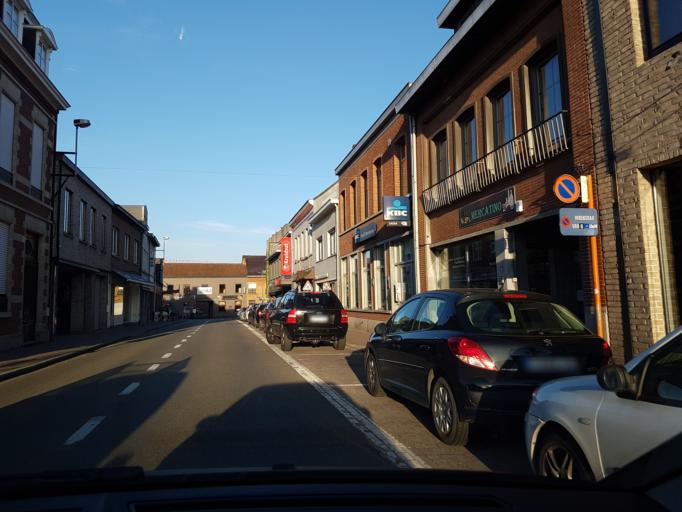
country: BE
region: Flanders
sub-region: Provincie Vlaams-Brabant
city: Merchtem
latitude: 50.9587
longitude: 4.2312
